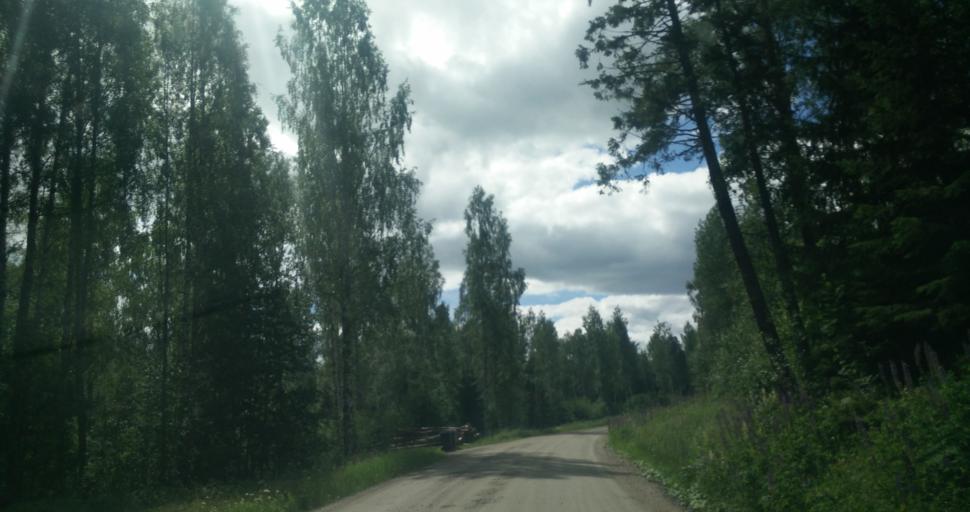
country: SE
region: Gaevleborg
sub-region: Nordanstigs Kommun
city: Bergsjoe
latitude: 62.1291
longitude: 17.1251
